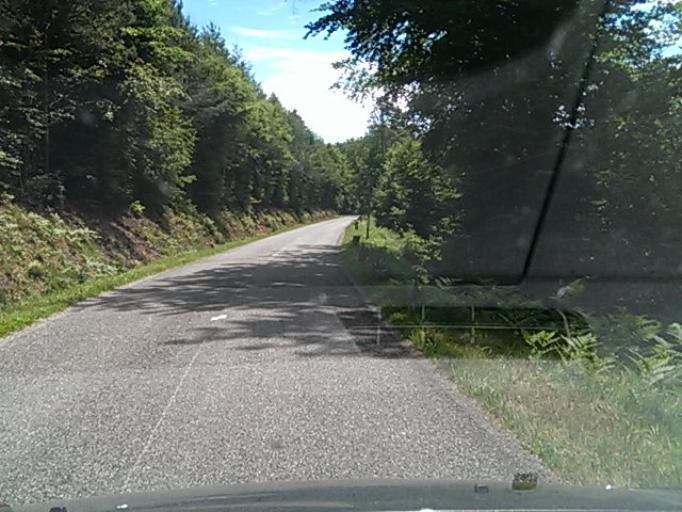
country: FR
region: Lorraine
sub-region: Departement de la Moselle
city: Soucht
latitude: 48.9330
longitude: 7.3652
